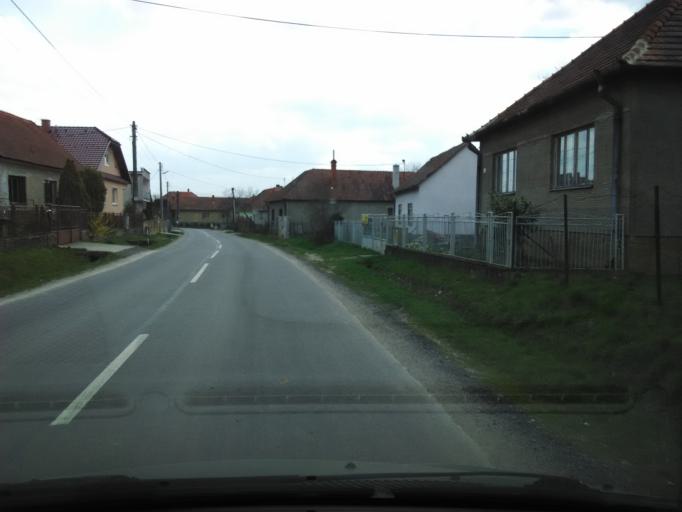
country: SK
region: Nitriansky
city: Zlate Moravce
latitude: 48.4122
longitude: 18.3047
